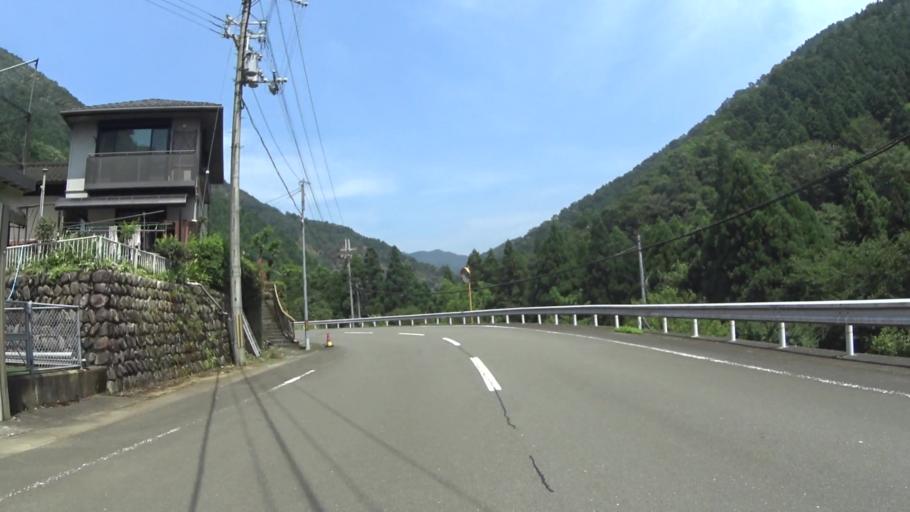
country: JP
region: Kyoto
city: Ayabe
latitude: 35.2875
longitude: 135.4270
